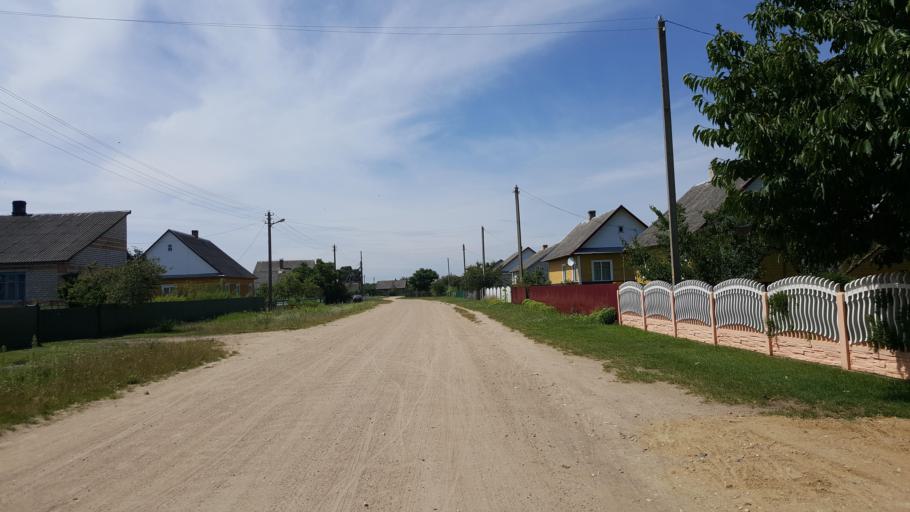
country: BY
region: Brest
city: Pruzhany
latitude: 52.5636
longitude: 24.2095
